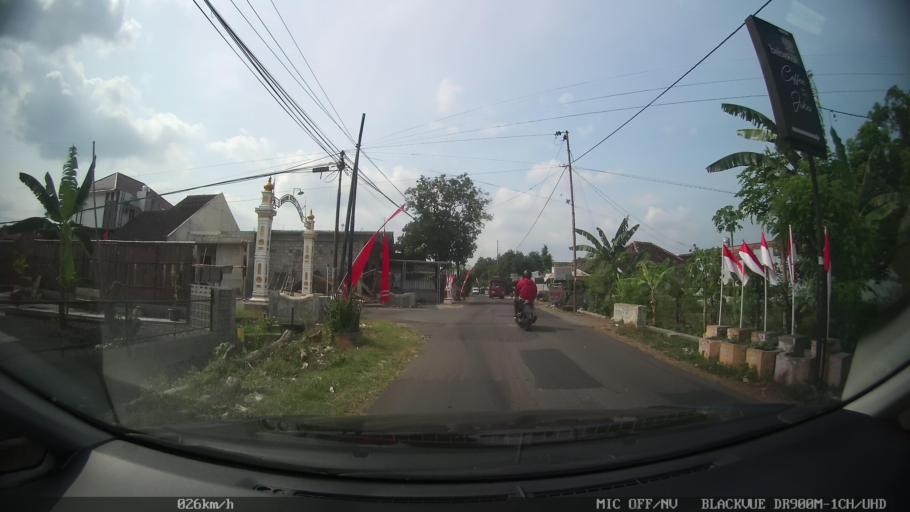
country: ID
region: Daerah Istimewa Yogyakarta
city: Depok
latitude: -7.7919
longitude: 110.4462
